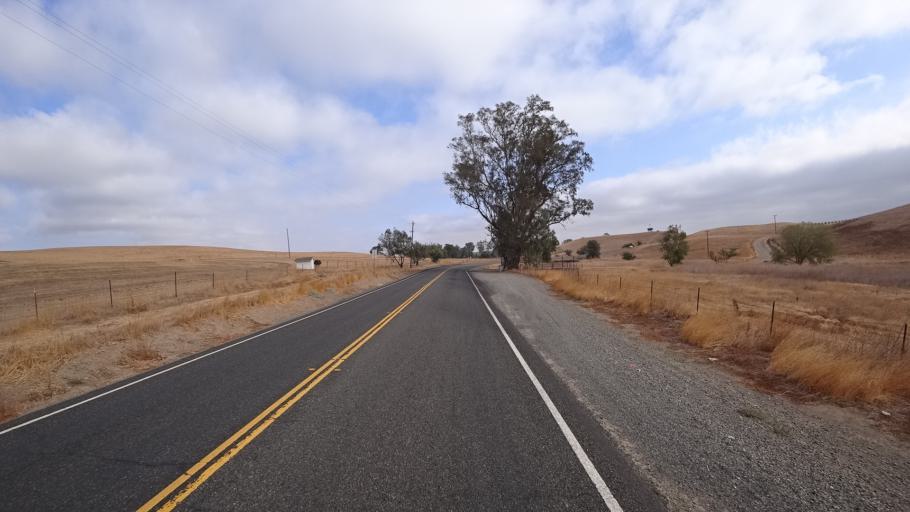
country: US
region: California
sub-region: Yolo County
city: Dunnigan
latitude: 38.7931
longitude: -121.9126
